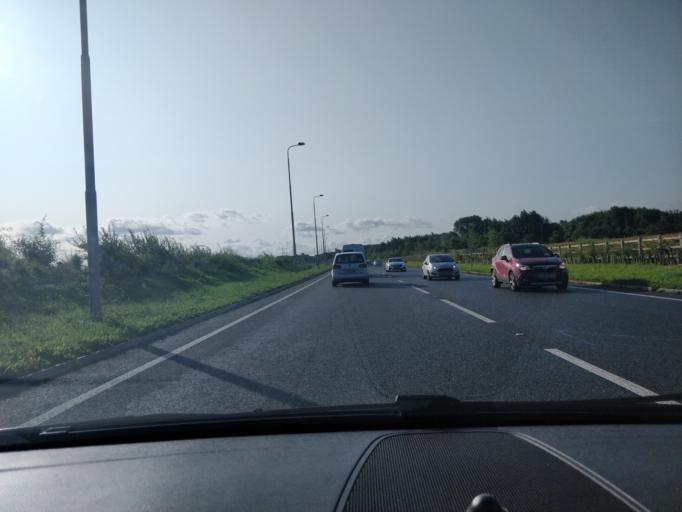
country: GB
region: England
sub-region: Sefton
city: Maghull
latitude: 53.4961
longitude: -2.9629
